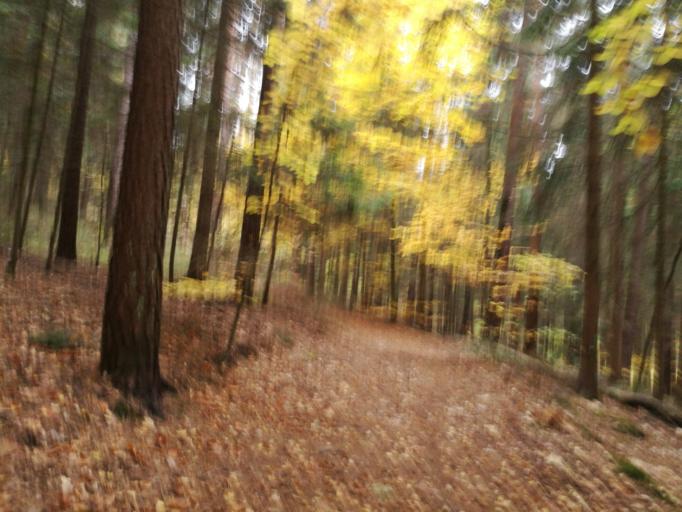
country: DE
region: Bavaria
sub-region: Regierungsbezirk Mittelfranken
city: Zirndorf
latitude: 49.4675
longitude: 10.9361
